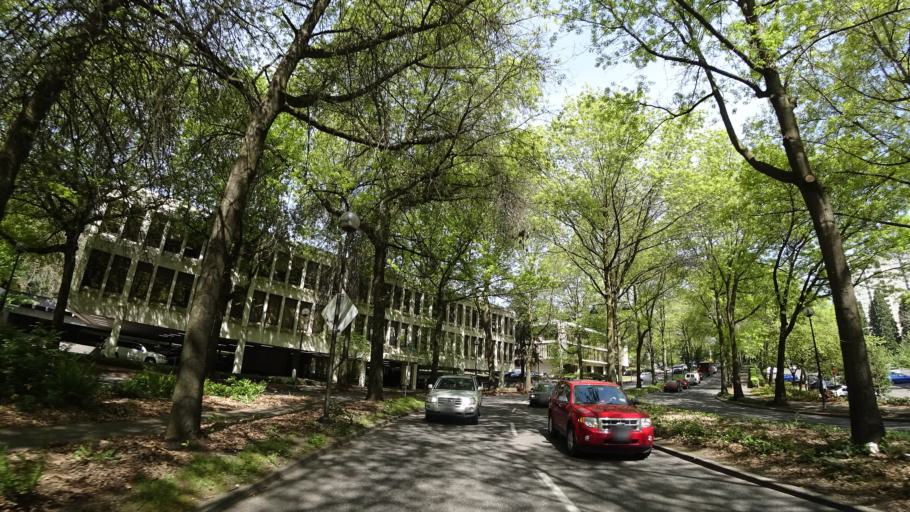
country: US
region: Oregon
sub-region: Multnomah County
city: Portland
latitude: 45.5039
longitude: -122.6808
